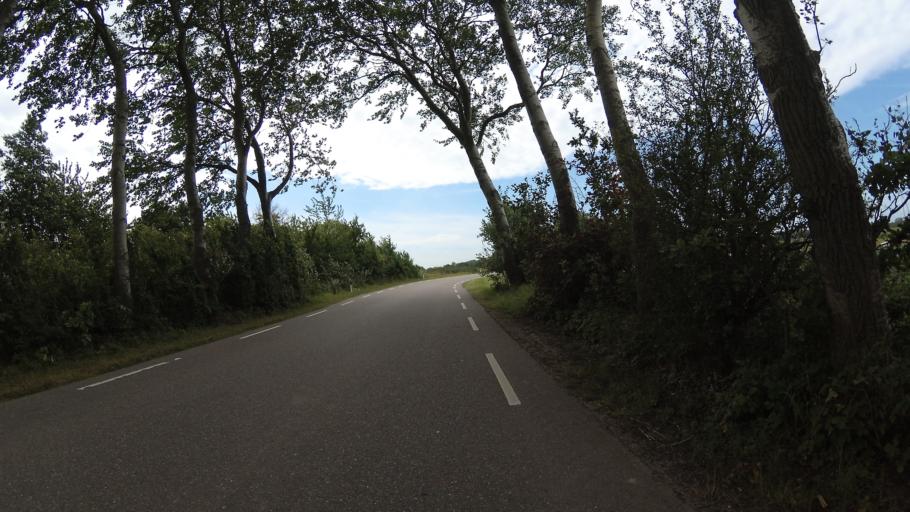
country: NL
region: Zeeland
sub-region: Gemeente Middelburg
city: Middelburg
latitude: 51.5754
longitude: 3.5748
